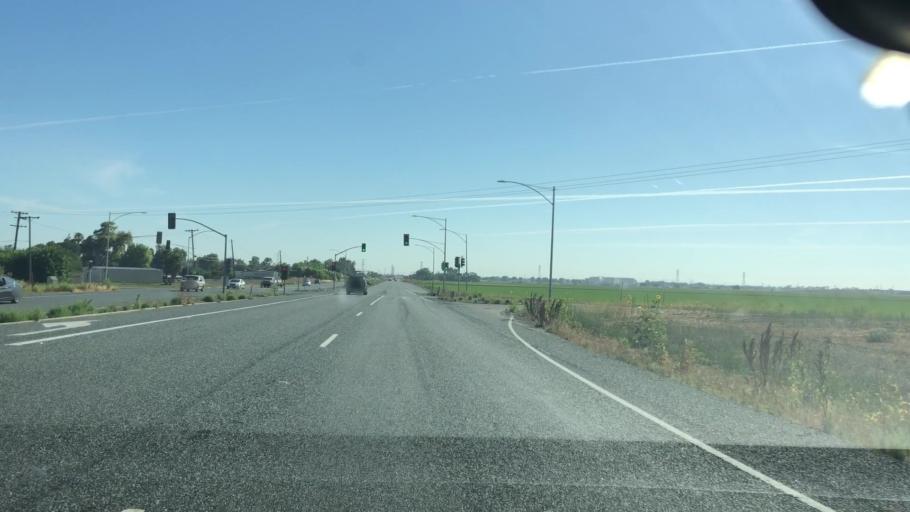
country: US
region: California
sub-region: San Joaquin County
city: Tracy
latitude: 37.7451
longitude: -121.3625
